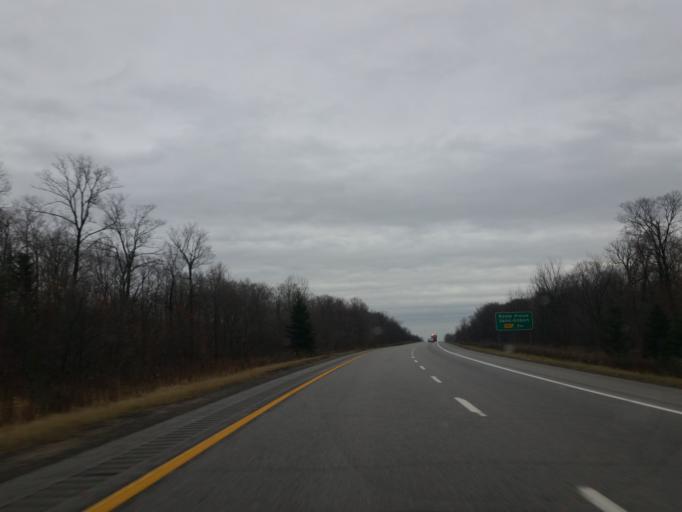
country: CA
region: Quebec
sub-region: Capitale-Nationale
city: Saint-Marc-des-Carrieres
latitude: 46.6567
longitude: -71.9705
